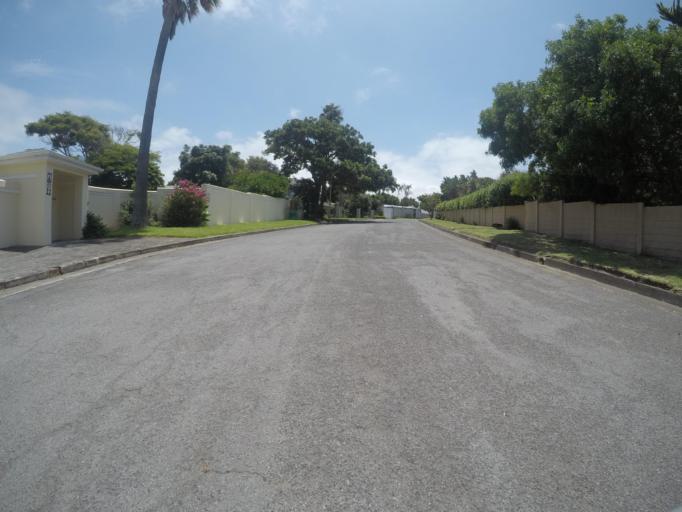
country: ZA
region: Eastern Cape
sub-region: Buffalo City Metropolitan Municipality
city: East London
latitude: -32.9966
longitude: 27.9219
